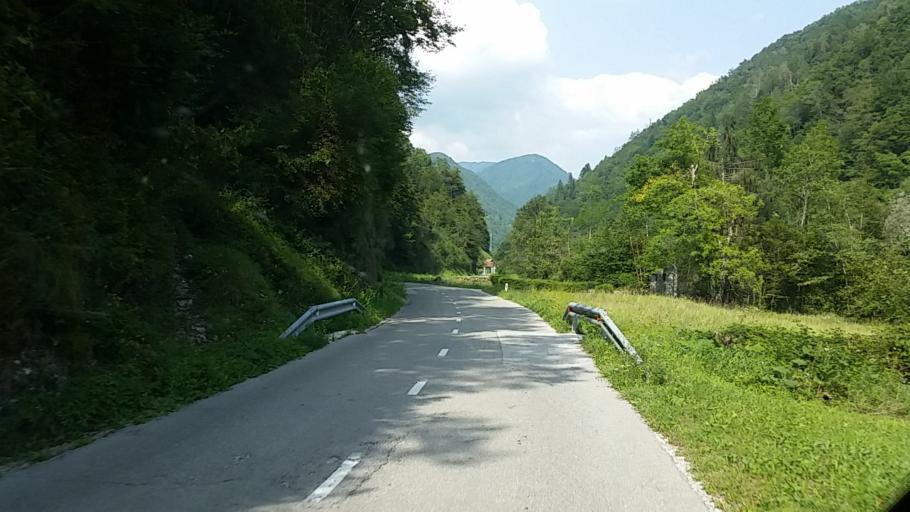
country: SI
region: Cerkno
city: Cerkno
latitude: 46.1819
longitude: 13.9209
